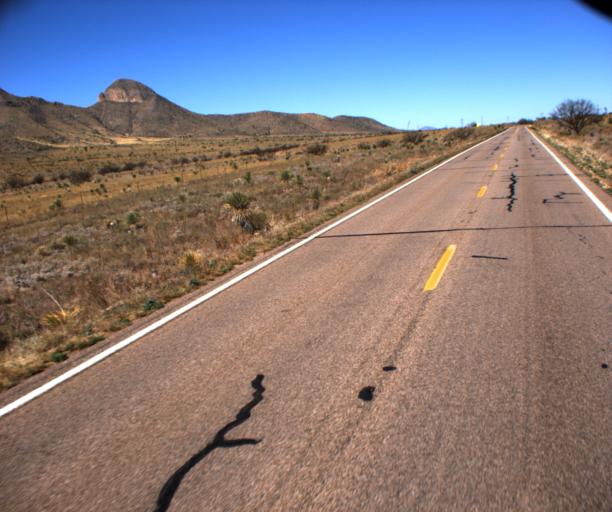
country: US
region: Arizona
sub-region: Cochise County
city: Huachuca City
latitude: 31.7154
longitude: -110.4655
